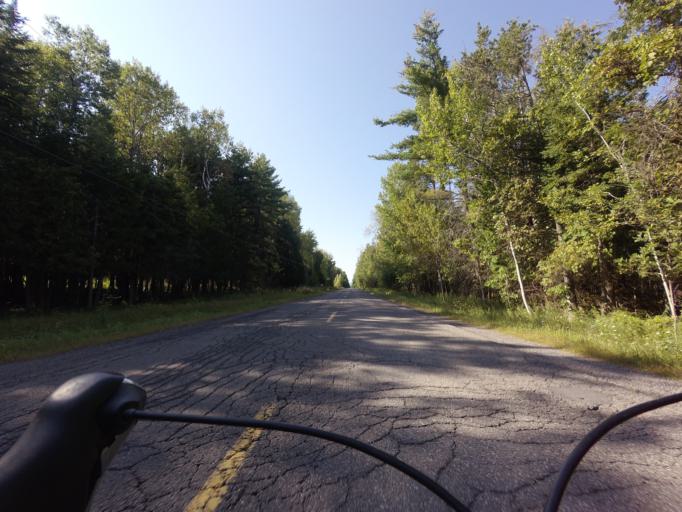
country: CA
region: Ontario
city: Bells Corners
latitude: 45.4721
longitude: -76.0145
